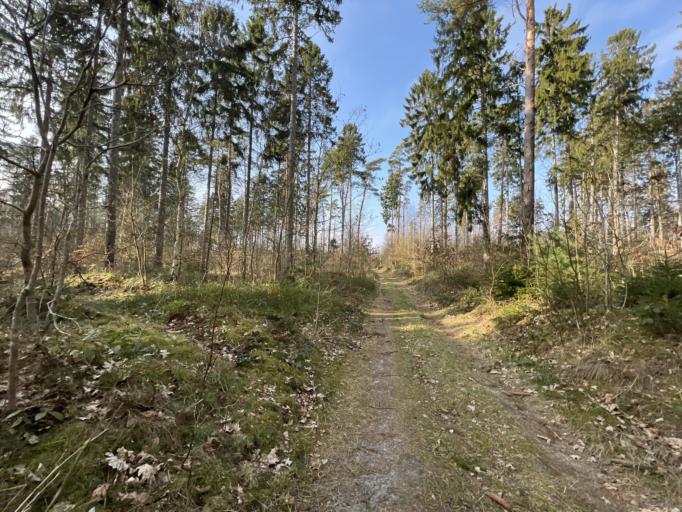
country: DE
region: Mecklenburg-Vorpommern
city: Sagard
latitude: 54.4793
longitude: 13.5573
